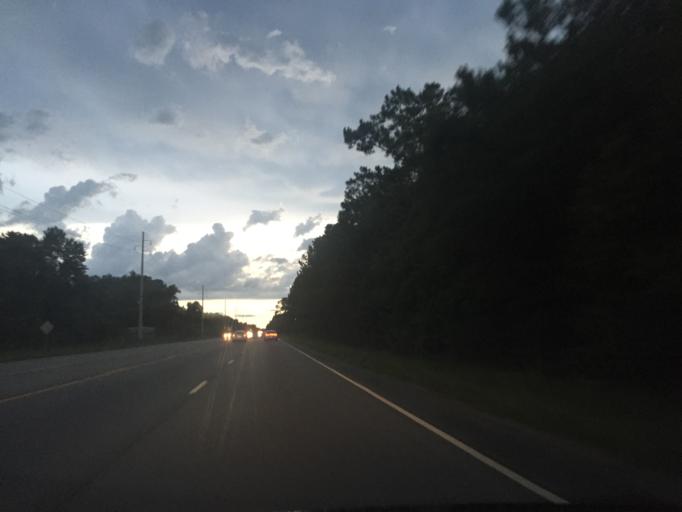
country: US
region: Georgia
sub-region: Liberty County
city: Hinesville
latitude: 31.8437
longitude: -81.5452
